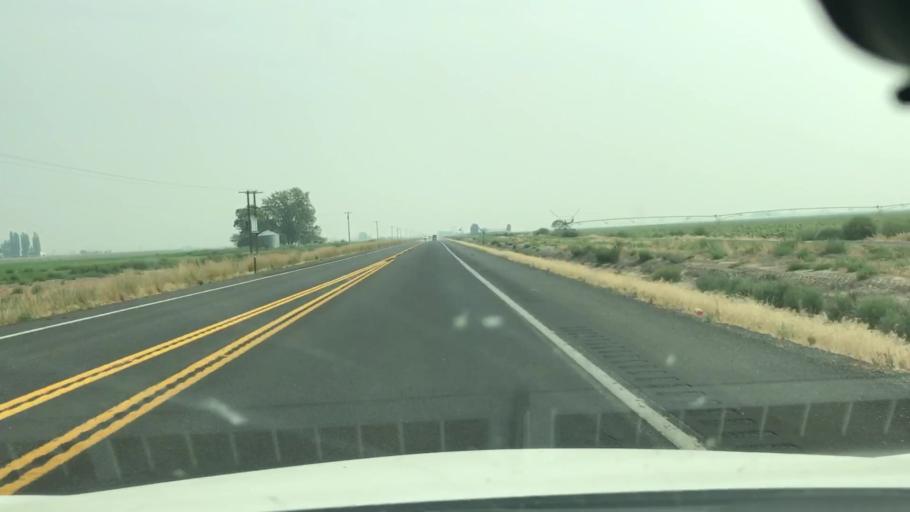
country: US
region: Washington
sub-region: Grant County
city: Quincy
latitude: 47.2341
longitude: -119.8081
